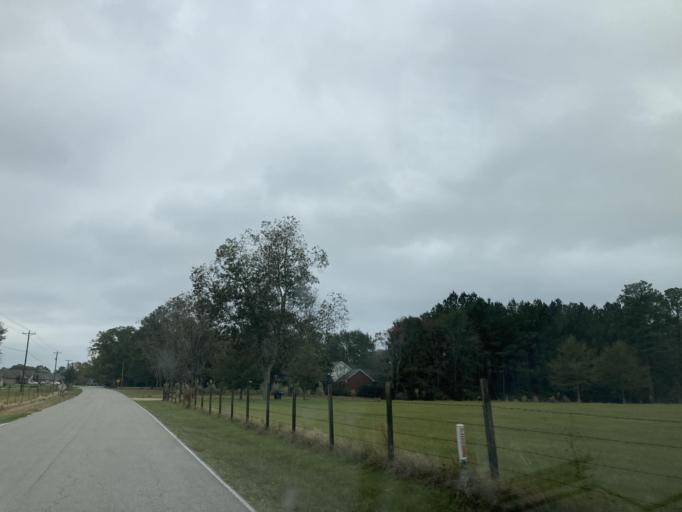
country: US
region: Mississippi
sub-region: Lamar County
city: Purvis
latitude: 31.1509
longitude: -89.4325
